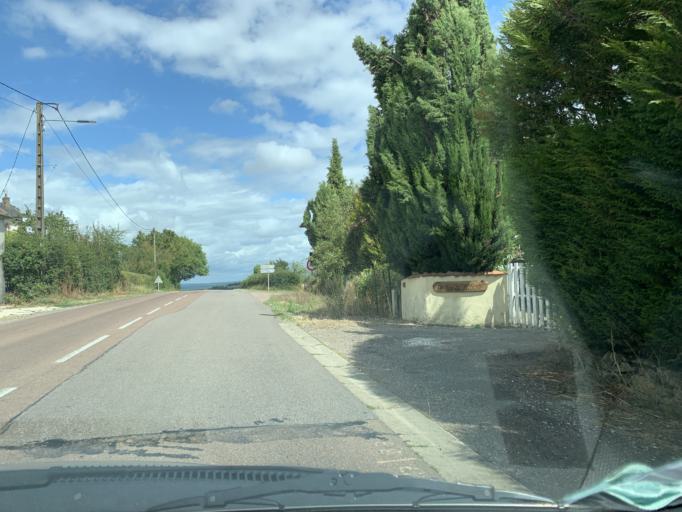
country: FR
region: Bourgogne
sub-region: Departement de la Nievre
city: Varzy
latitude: 47.3763
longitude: 3.4301
